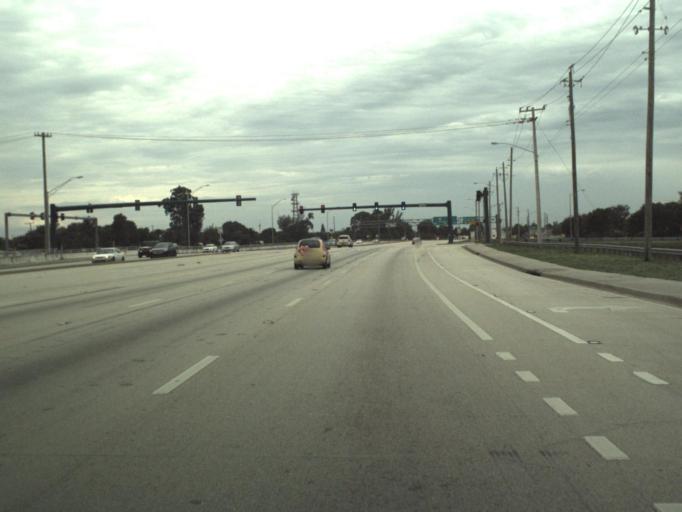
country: US
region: Florida
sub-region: Palm Beach County
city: Haverhill
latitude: 26.6776
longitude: -80.1025
